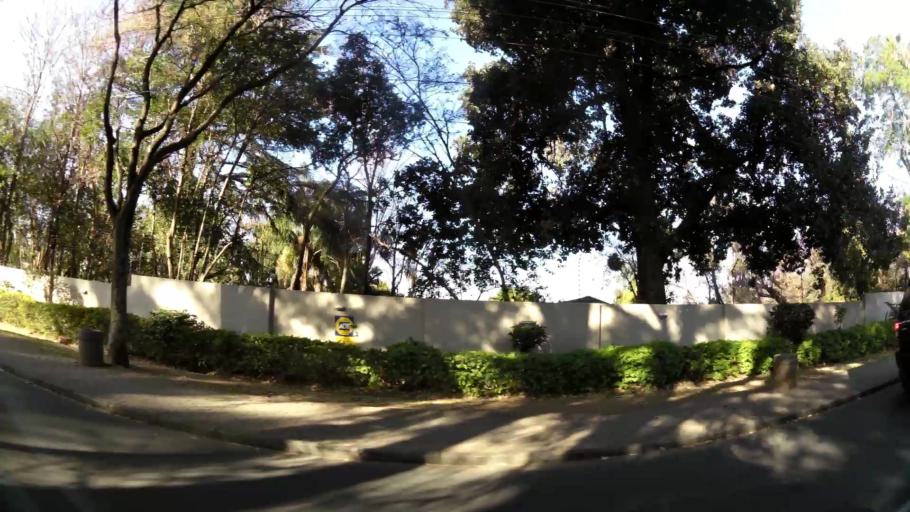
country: ZA
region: Gauteng
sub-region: City of Johannesburg Metropolitan Municipality
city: Johannesburg
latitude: -26.1135
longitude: 28.0704
